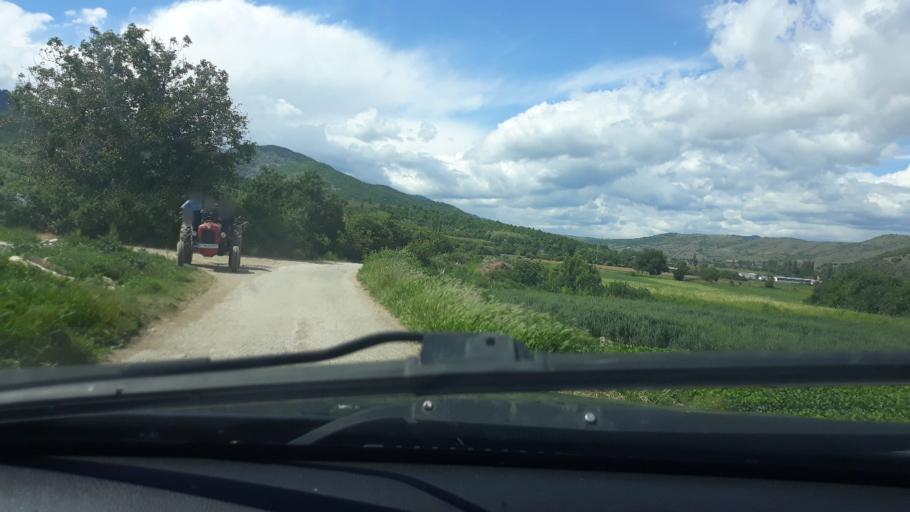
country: MK
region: Krivogastani
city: Krivogashtani
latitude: 41.3403
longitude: 21.3001
